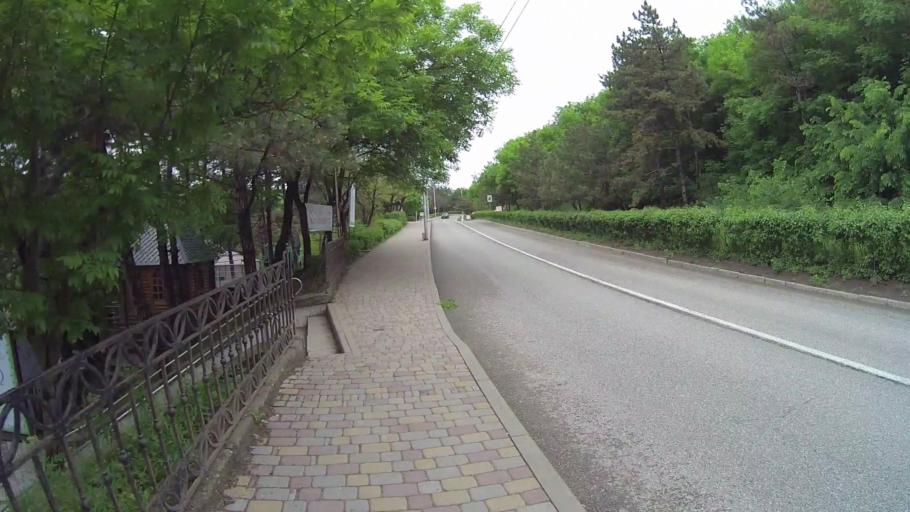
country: RU
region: Stavropol'skiy
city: Goryachevodskiy
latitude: 44.0408
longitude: 43.0886
